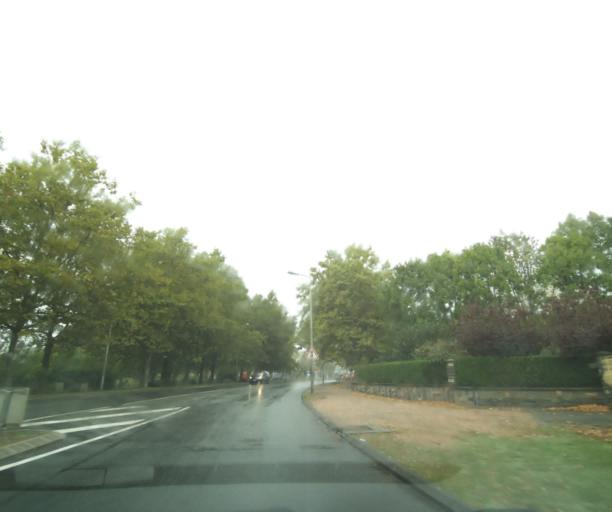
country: FR
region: Auvergne
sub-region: Departement du Puy-de-Dome
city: Cebazat
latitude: 45.8291
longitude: 3.1058
